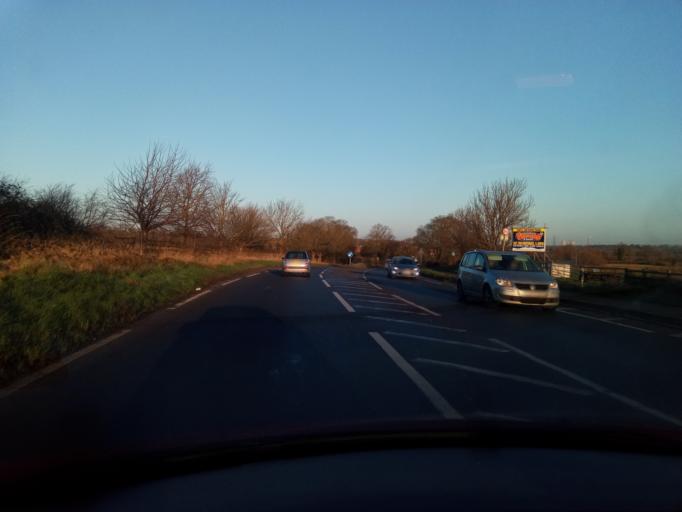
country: GB
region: England
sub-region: Leicestershire
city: Hathern
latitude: 52.7863
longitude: -1.2479
